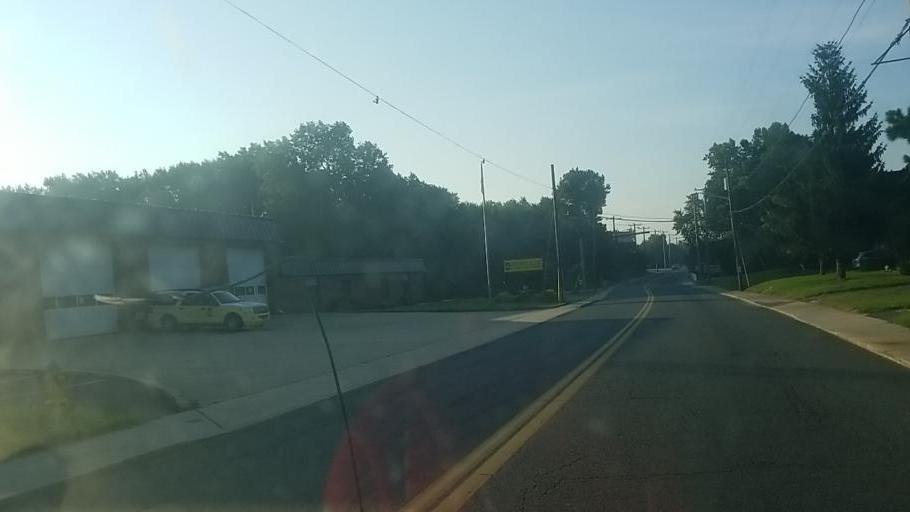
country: US
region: Delaware
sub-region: Sussex County
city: Selbyville
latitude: 38.4635
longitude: -75.2236
